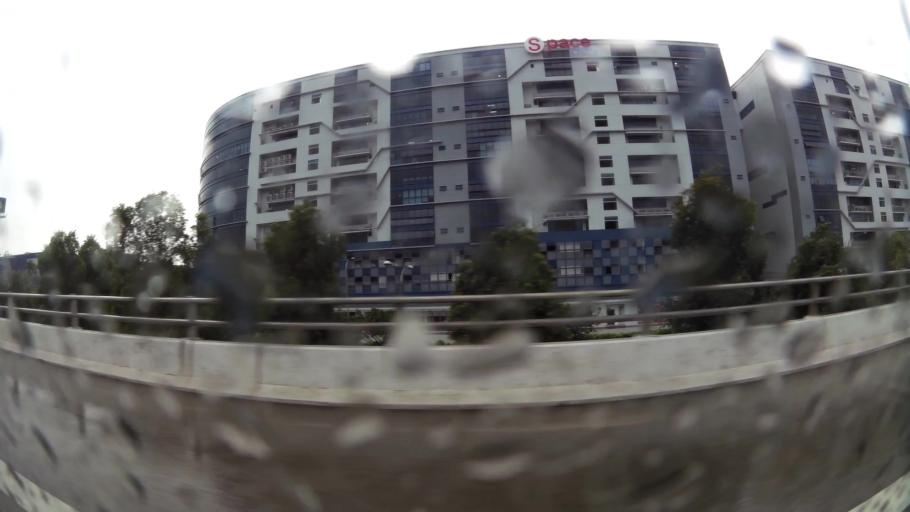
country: MY
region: Johor
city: Kampung Pasir Gudang Baru
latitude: 1.3762
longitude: 103.9308
